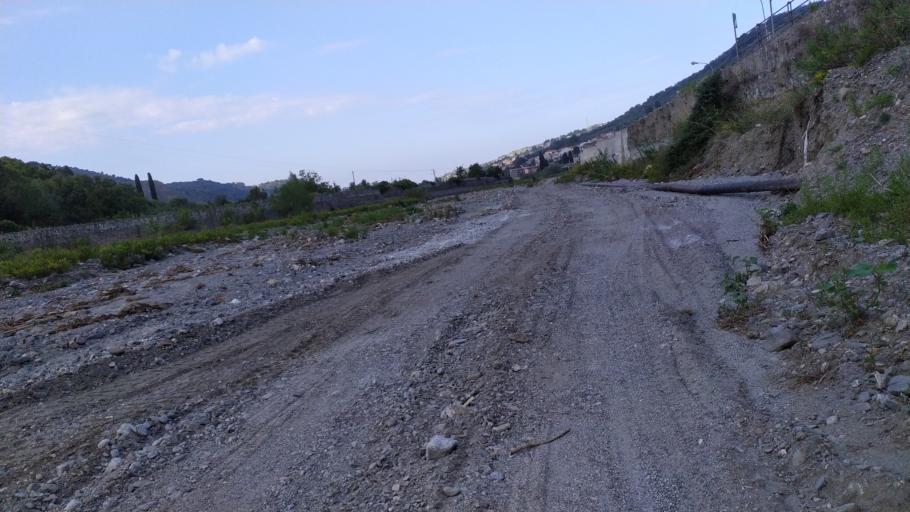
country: IT
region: Sicily
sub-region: Messina
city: Saponara
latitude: 38.1988
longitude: 15.4298
